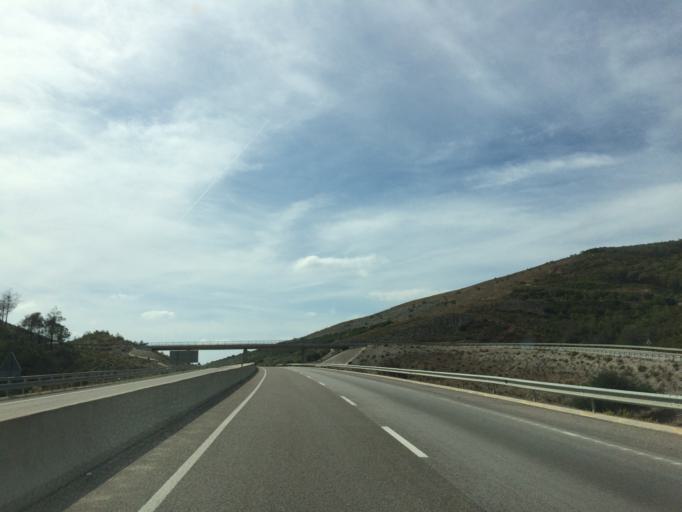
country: MA
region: Tanger-Tetouan
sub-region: Tanger-Assilah
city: Tangier
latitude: 35.7955
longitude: -5.5903
